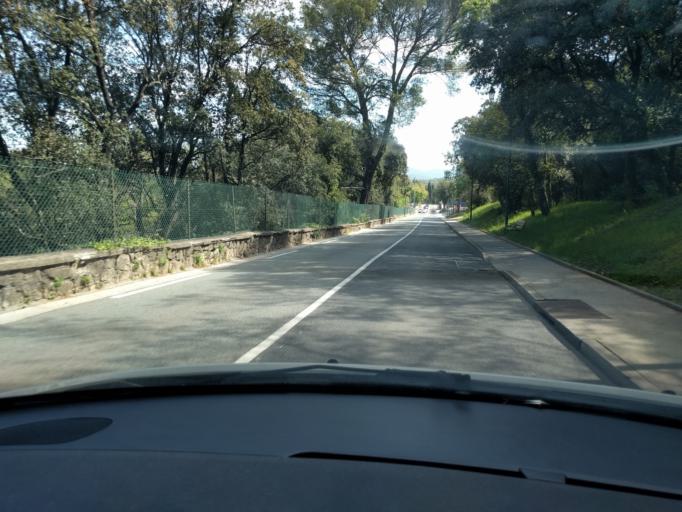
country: FR
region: Provence-Alpes-Cote d'Azur
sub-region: Departement du Var
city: Pierrefeu-du-Var
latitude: 43.2300
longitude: 6.1470
